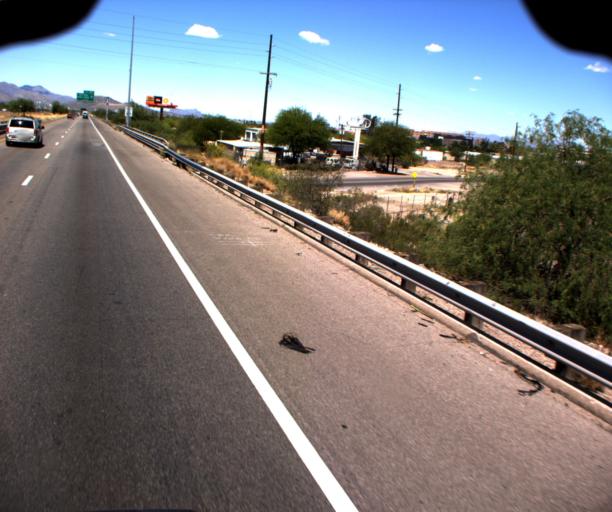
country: US
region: Arizona
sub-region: Pima County
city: South Tucson
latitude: 32.1669
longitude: -110.9258
